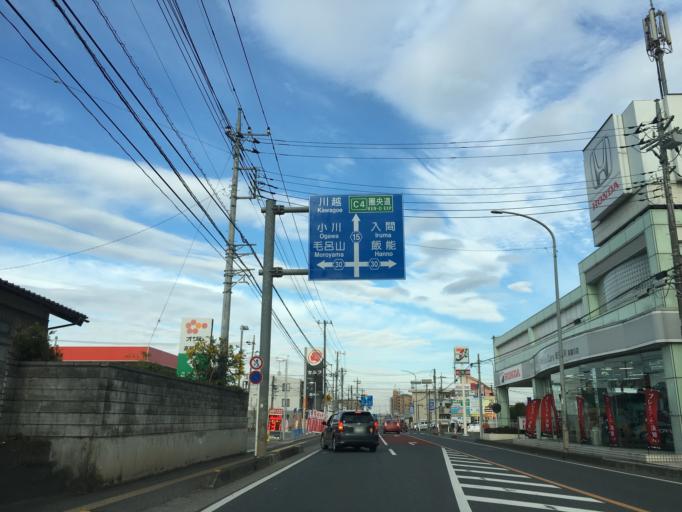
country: JP
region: Saitama
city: Hanno
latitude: 35.8916
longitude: 139.3341
